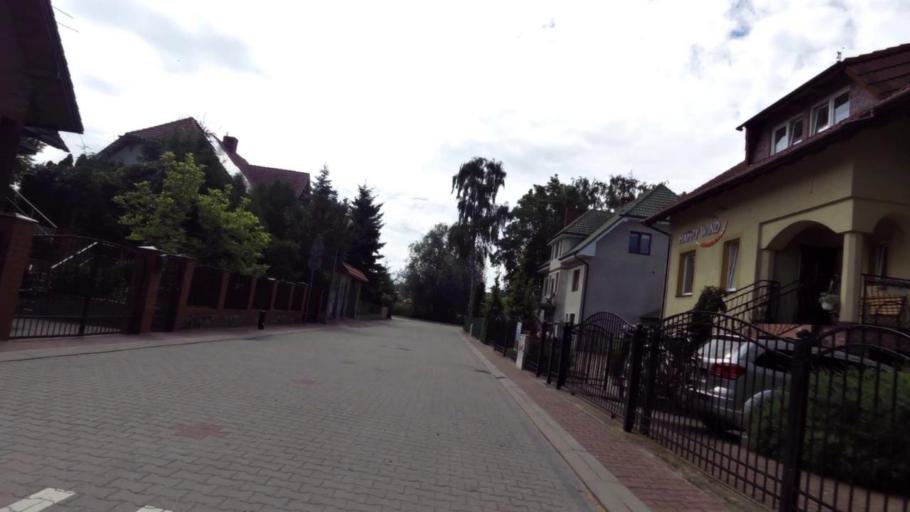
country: PL
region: West Pomeranian Voivodeship
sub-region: Powiat kamienski
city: Dziwnow
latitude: 54.0215
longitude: 14.7420
